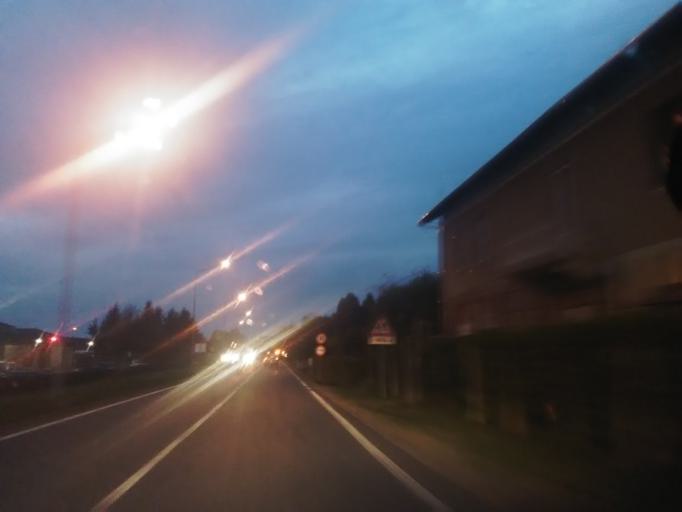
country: IT
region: Piedmont
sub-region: Provincia di Vercelli
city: Lozzolo
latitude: 45.6089
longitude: 8.3249
